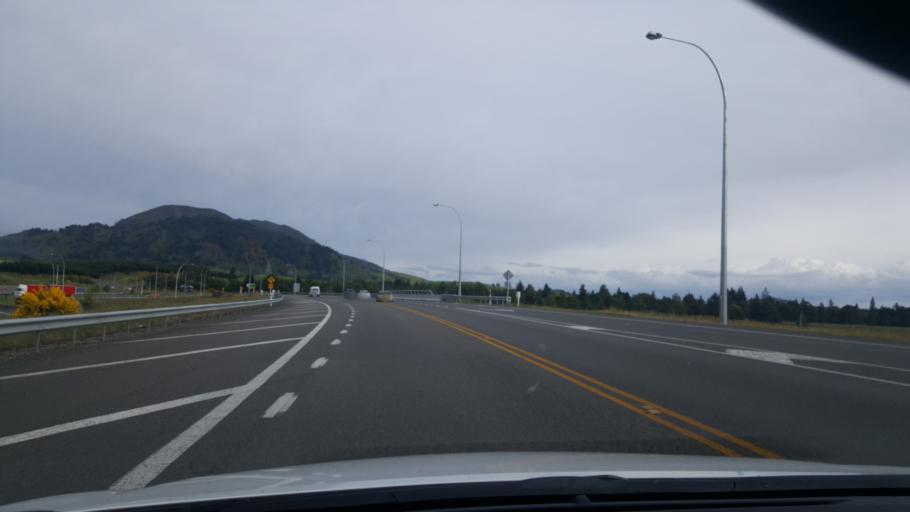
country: NZ
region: Waikato
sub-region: Taupo District
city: Taupo
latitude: -38.6678
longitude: 176.1034
